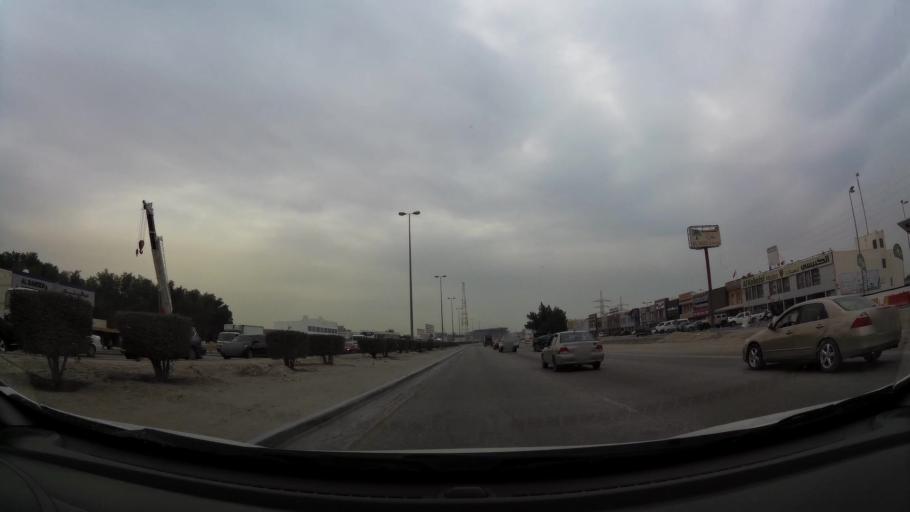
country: BH
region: Northern
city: Sitrah
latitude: 26.1280
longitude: 50.5974
